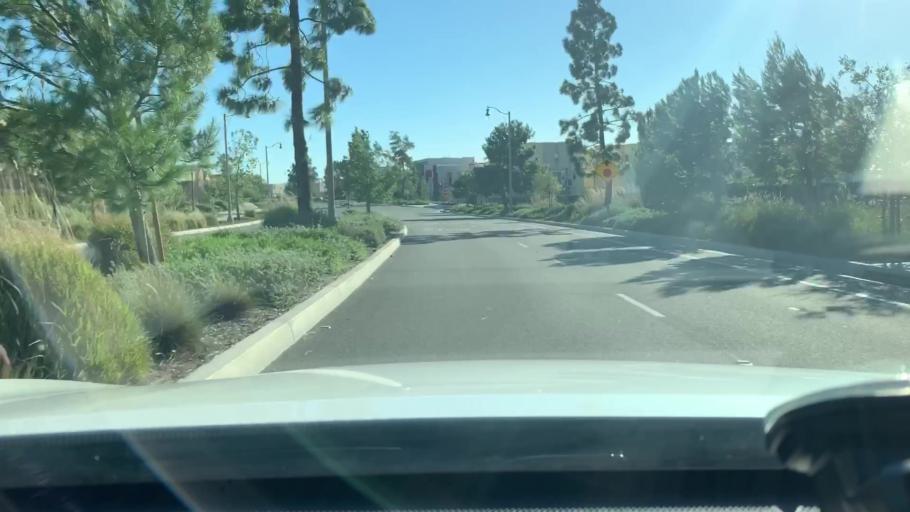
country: US
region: California
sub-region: Orange County
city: Lake Forest
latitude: 33.6888
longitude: -117.7387
